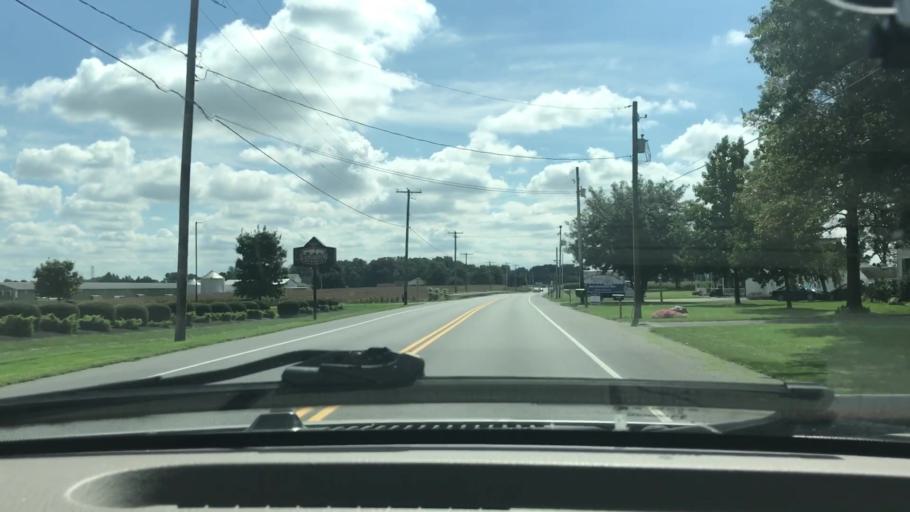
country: US
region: Pennsylvania
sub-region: Lancaster County
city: Manheim
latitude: 40.1322
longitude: -76.3808
